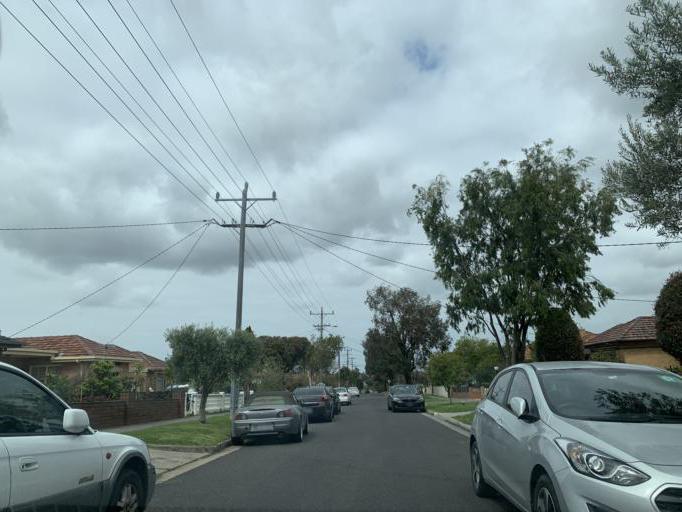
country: AU
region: Victoria
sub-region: Moreland
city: Pascoe Vale South
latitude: -37.7425
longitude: 144.9408
